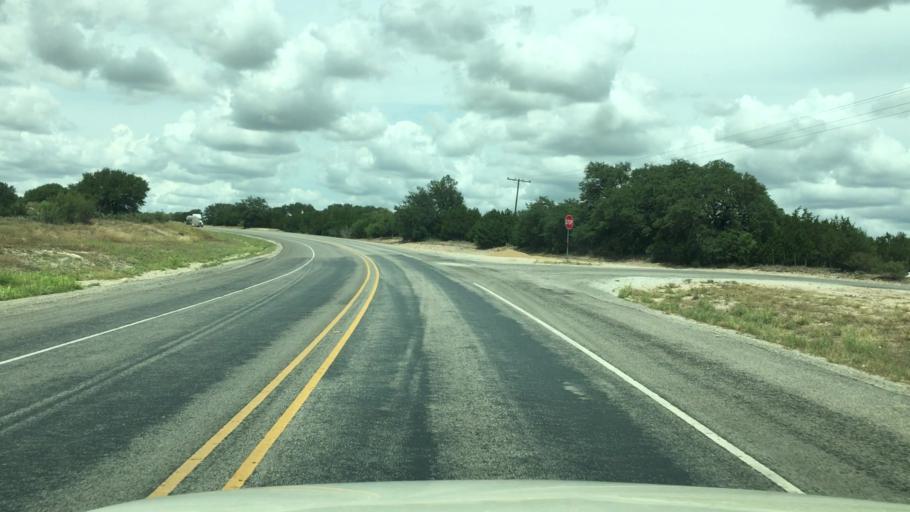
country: US
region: Texas
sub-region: McCulloch County
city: Brady
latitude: 31.0174
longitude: -99.2111
